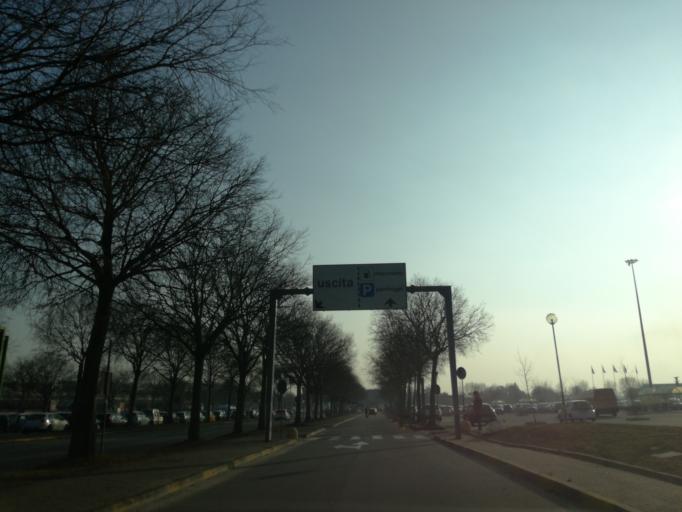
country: IT
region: Piedmont
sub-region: Provincia di Torino
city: Lesna
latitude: 45.0559
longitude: 7.6147
